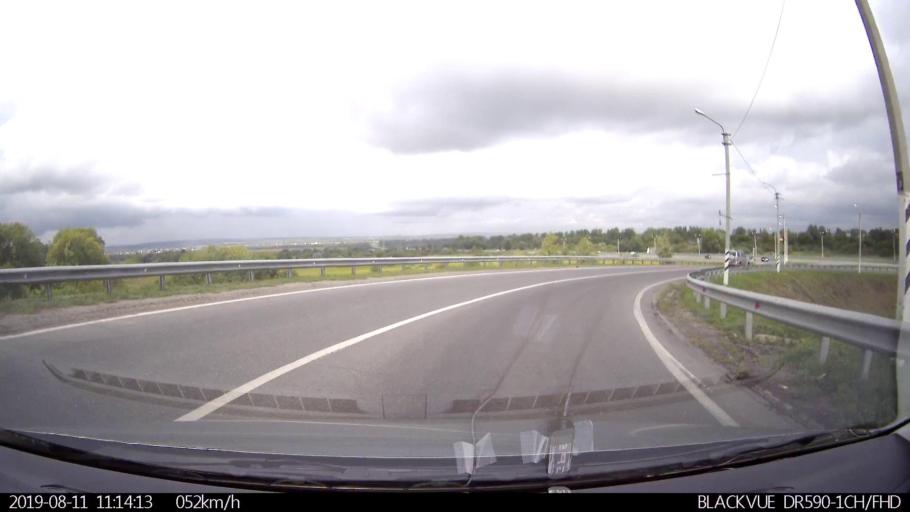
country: RU
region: Ulyanovsk
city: Novoul'yanovsk
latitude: 54.2107
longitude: 48.2925
